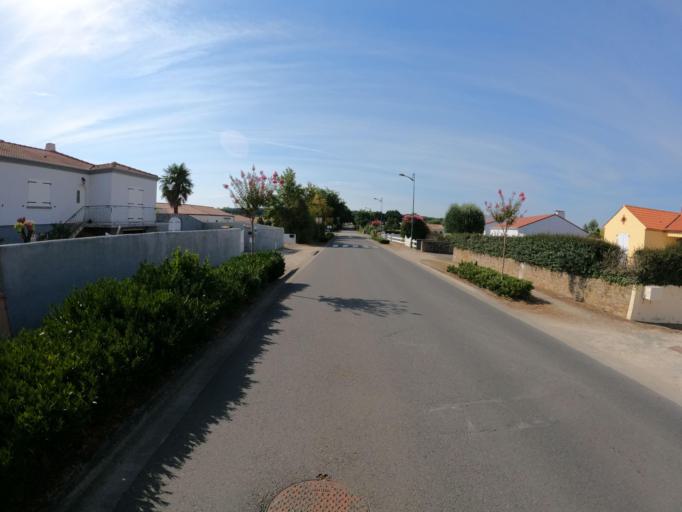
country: FR
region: Pays de la Loire
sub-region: Departement de la Vendee
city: Falleron
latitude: 46.8780
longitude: -1.7037
